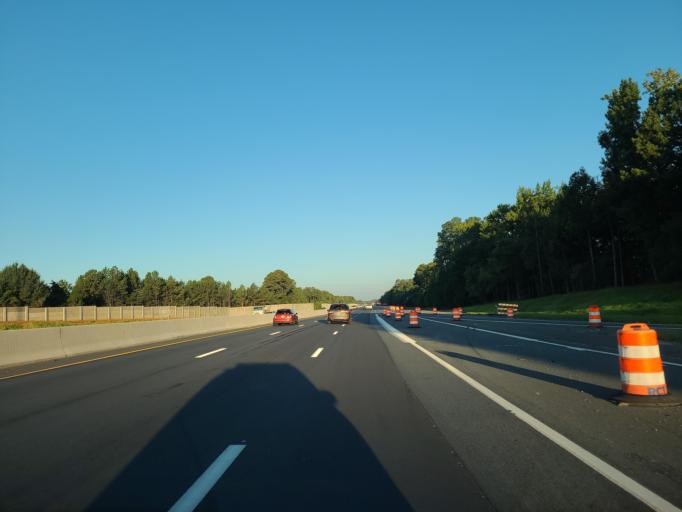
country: US
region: North Carolina
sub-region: Union County
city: Weddington
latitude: 35.0602
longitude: -80.7726
